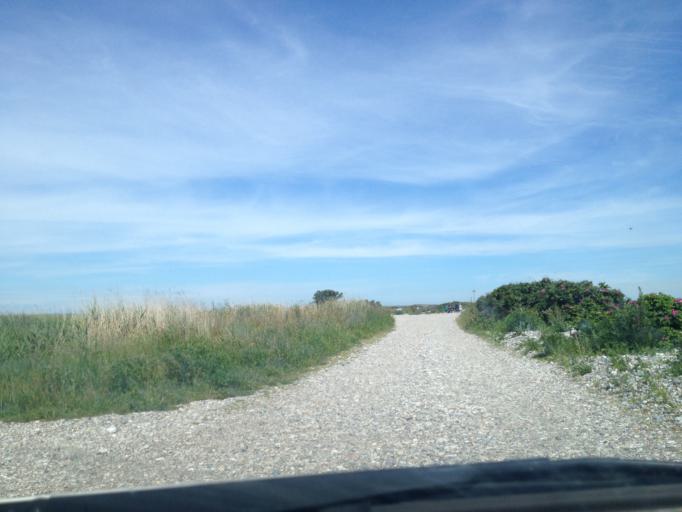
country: DK
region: Central Jutland
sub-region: Samso Kommune
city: Tranebjerg
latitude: 55.8821
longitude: 10.6776
